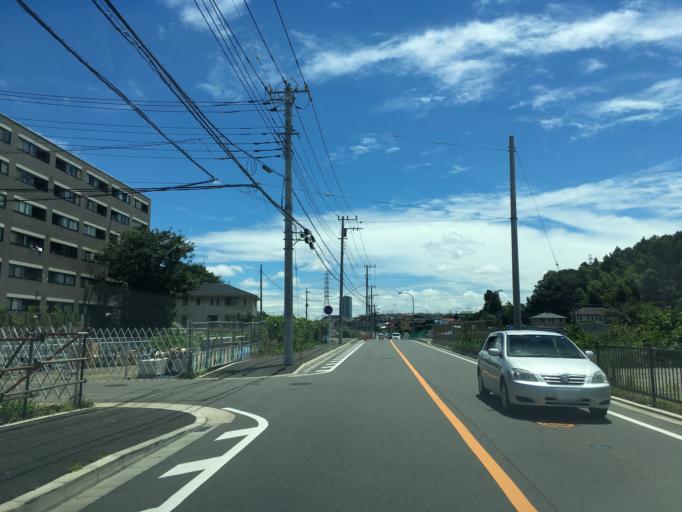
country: JP
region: Tokyo
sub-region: Machida-shi
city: Machida
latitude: 35.5502
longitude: 139.4907
